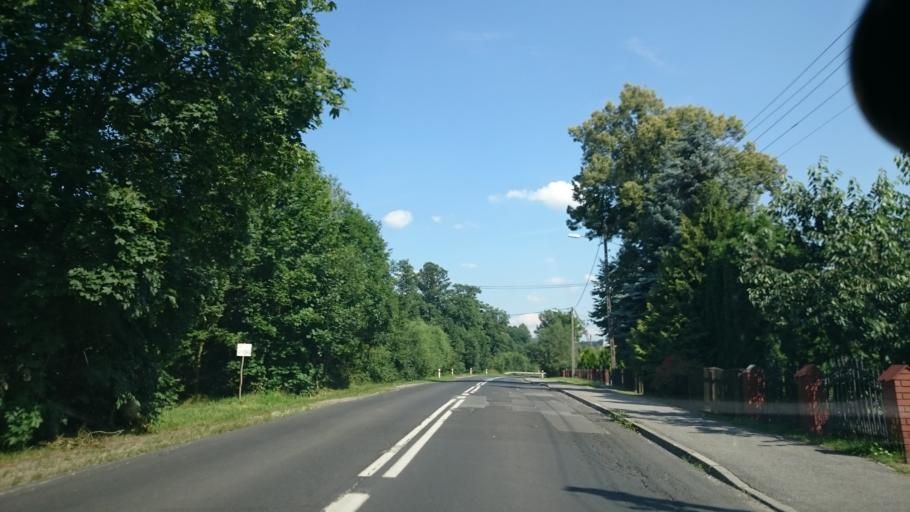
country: PL
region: Lower Silesian Voivodeship
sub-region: Powiat klodzki
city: Ladek-Zdroj
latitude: 50.3458
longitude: 16.7946
